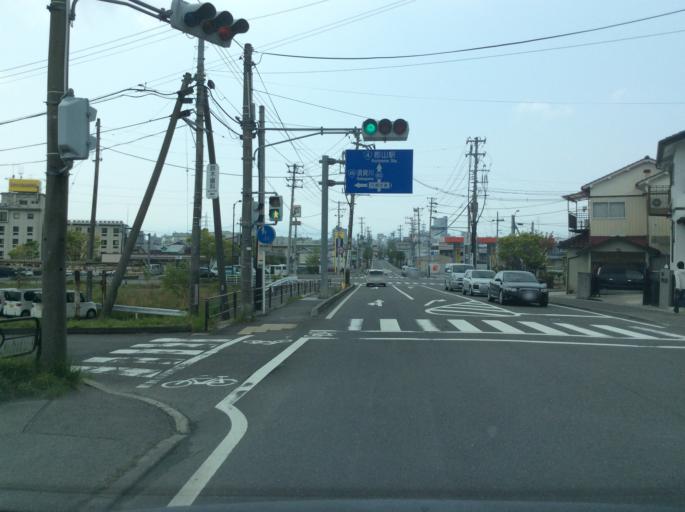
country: JP
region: Fukushima
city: Koriyama
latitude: 37.3874
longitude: 140.4003
